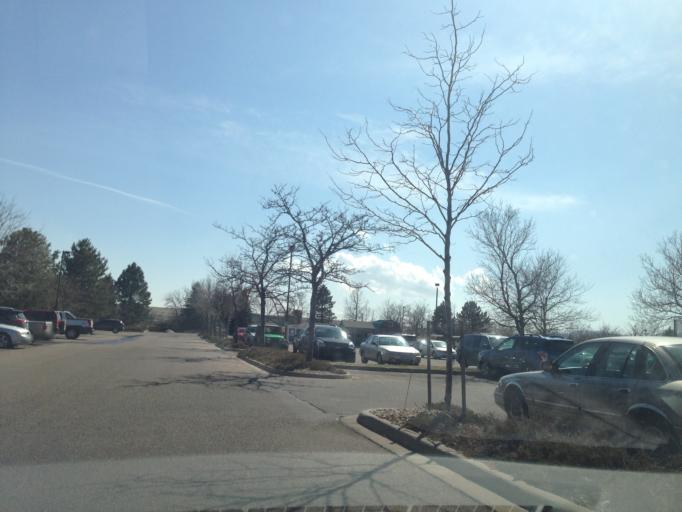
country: US
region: Colorado
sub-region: Boulder County
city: Superior
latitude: 39.9612
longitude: -105.1685
